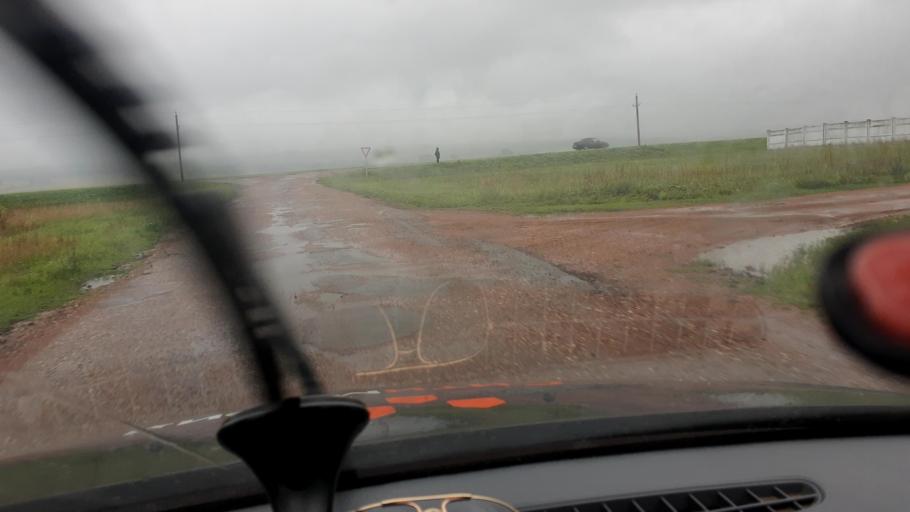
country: RU
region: Bashkortostan
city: Karmaskaly
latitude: 53.9894
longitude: 56.3968
